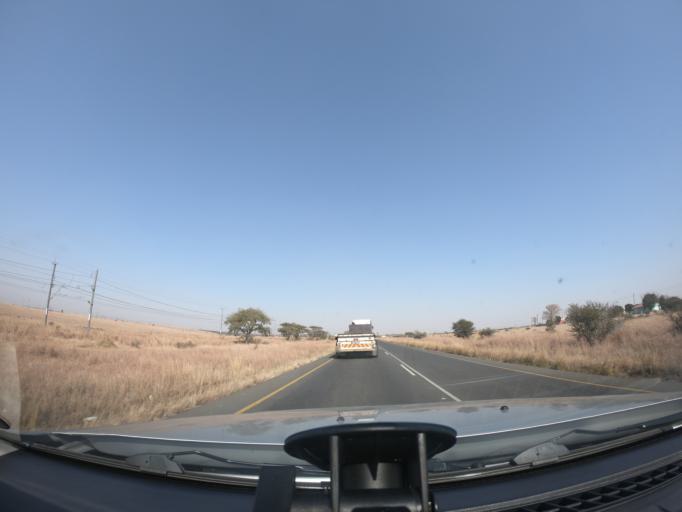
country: ZA
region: KwaZulu-Natal
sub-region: uThukela District Municipality
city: Ladysmith
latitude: -28.7567
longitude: 29.8216
